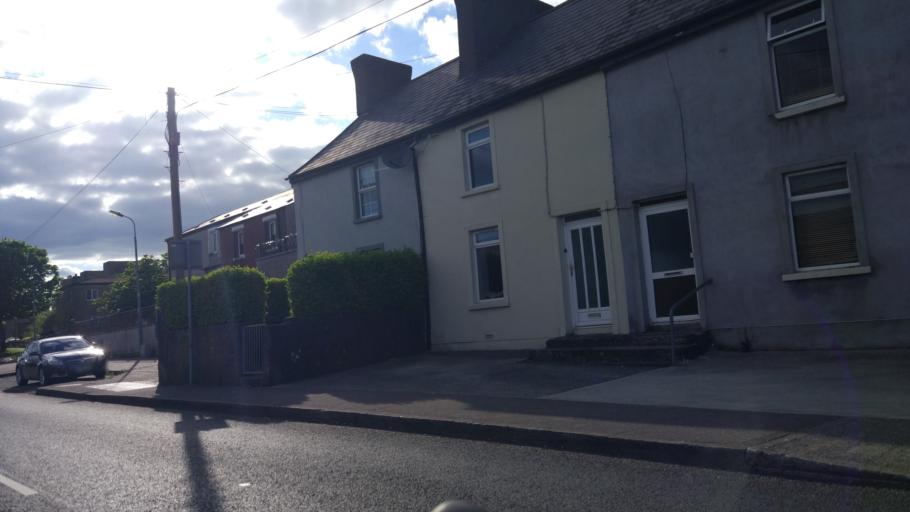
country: IE
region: Munster
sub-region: County Cork
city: Cork
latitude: 51.9135
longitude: -8.4332
